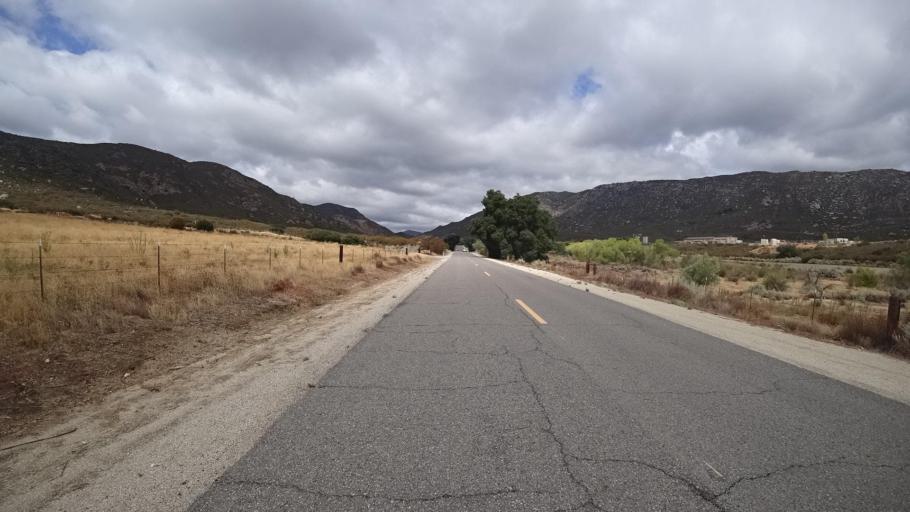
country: US
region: California
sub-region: San Diego County
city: Pine Valley
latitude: 32.7615
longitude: -116.4930
